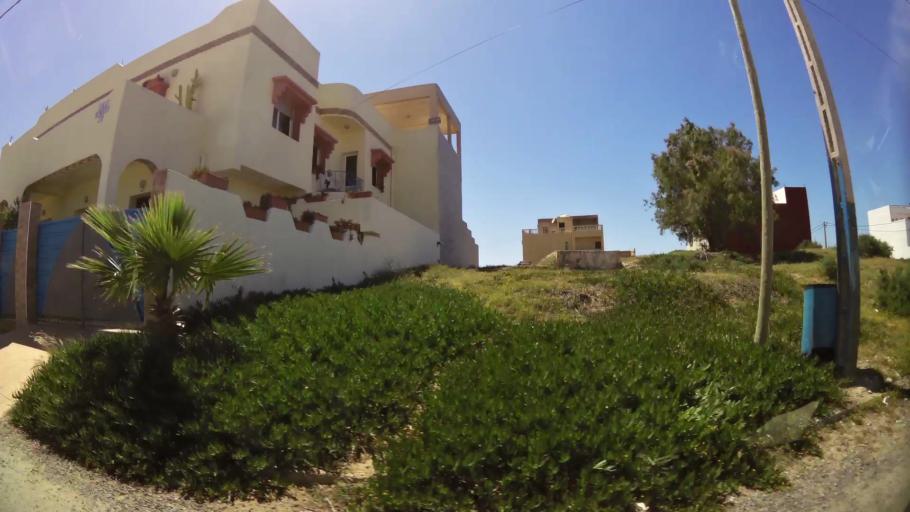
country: MA
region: Oriental
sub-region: Berkane-Taourirt
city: Madagh
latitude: 35.1426
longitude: -2.4261
